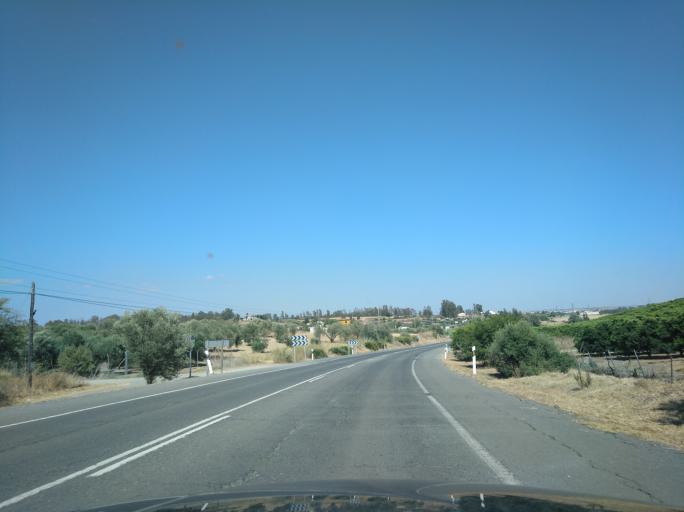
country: ES
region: Andalusia
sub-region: Provincia de Huelva
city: Gibraleon
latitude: 37.3543
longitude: -7.0082
